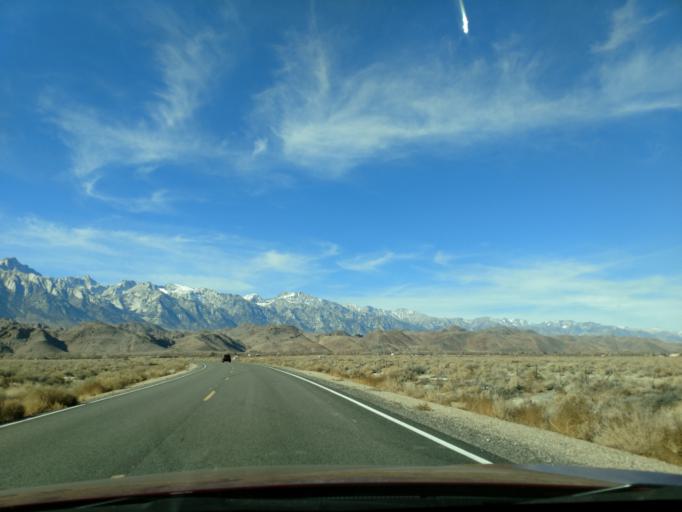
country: US
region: California
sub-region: Inyo County
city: Lone Pine
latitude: 36.5789
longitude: -118.0359
